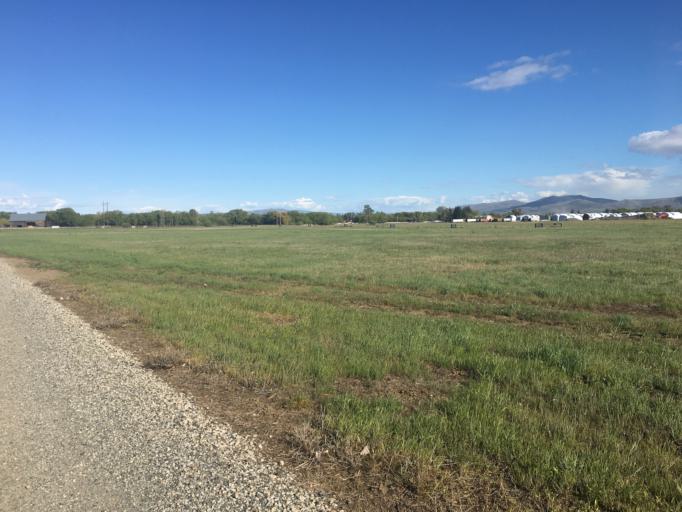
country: US
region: Washington
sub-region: Kittitas County
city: Ellensburg
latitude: 46.9905
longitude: -120.5650
